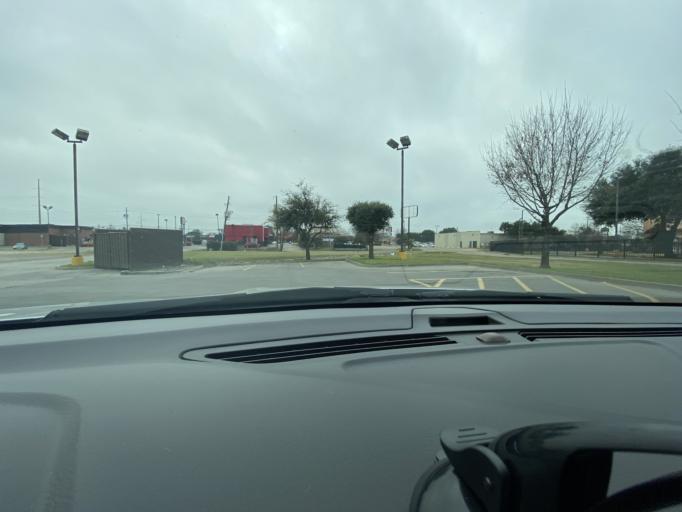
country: US
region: Texas
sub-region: Dallas County
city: Highland Park
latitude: 32.7931
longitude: -96.7012
